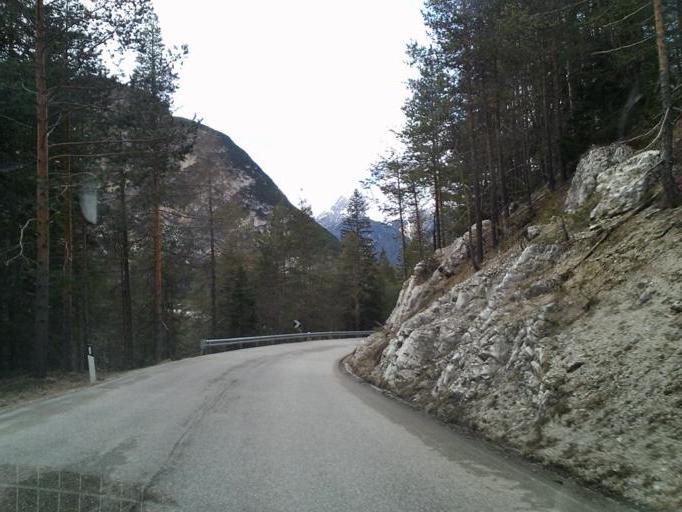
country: IT
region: Veneto
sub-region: Provincia di Belluno
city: Cortina d'Ampezzo
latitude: 46.6112
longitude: 12.2301
